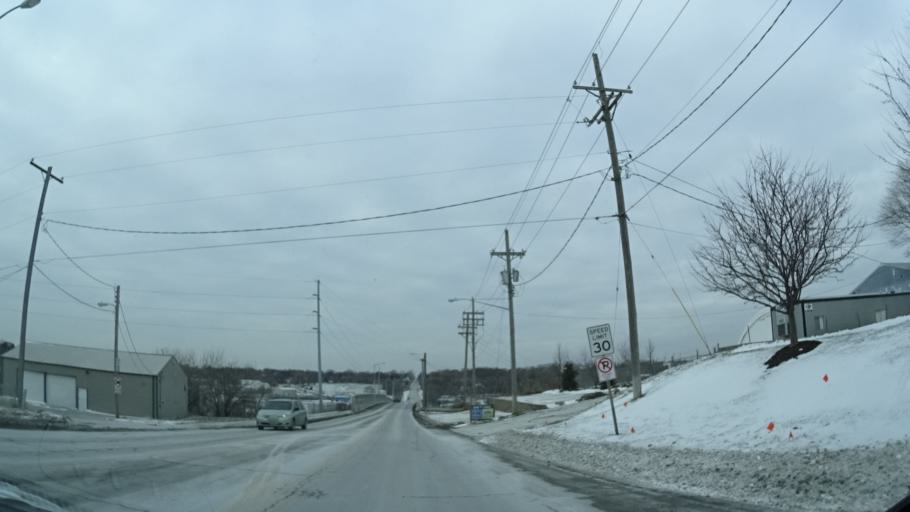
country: US
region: Nebraska
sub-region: Douglas County
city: Omaha
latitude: 41.2198
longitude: -95.9548
